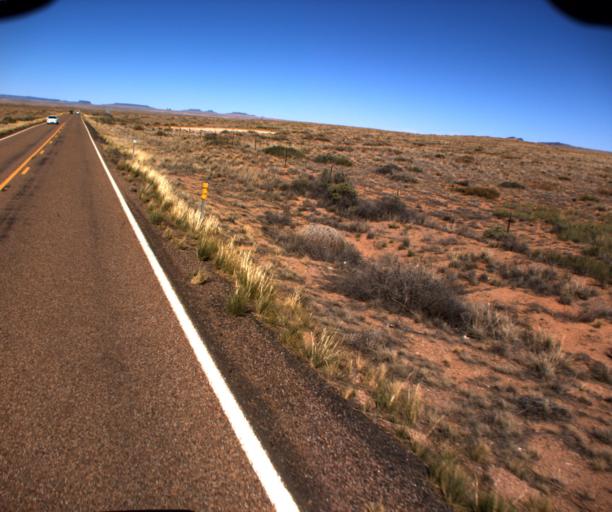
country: US
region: Arizona
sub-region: Navajo County
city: Holbrook
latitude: 35.0077
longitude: -110.0897
